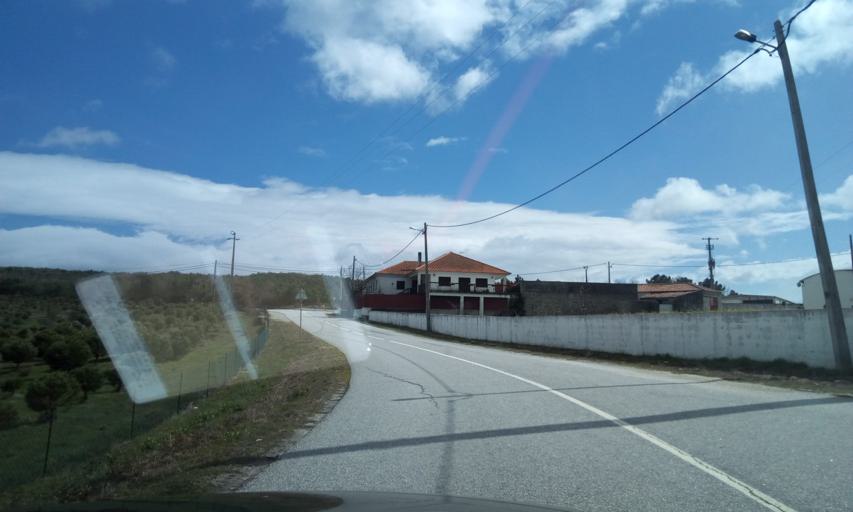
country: PT
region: Guarda
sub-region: Fornos de Algodres
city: Fornos de Algodres
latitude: 40.6398
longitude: -7.5489
